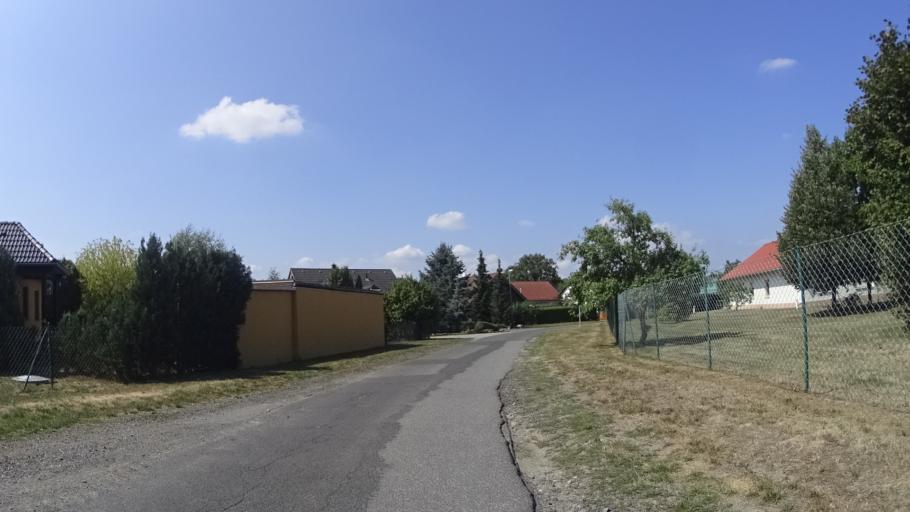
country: DE
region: Saxony
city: Gross Duben
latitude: 51.6060
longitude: 14.5099
